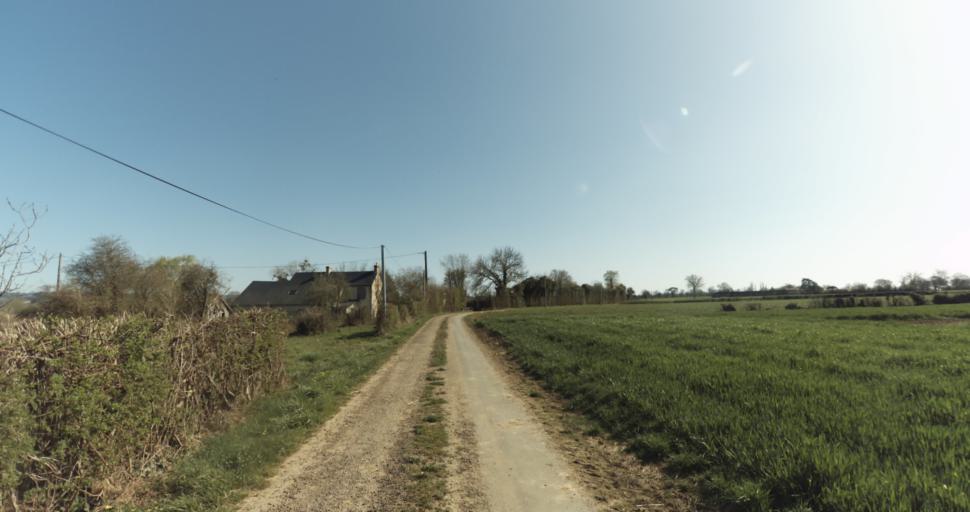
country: FR
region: Lower Normandy
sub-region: Departement du Calvados
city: Saint-Pierre-sur-Dives
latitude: 48.9346
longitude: -0.0059
